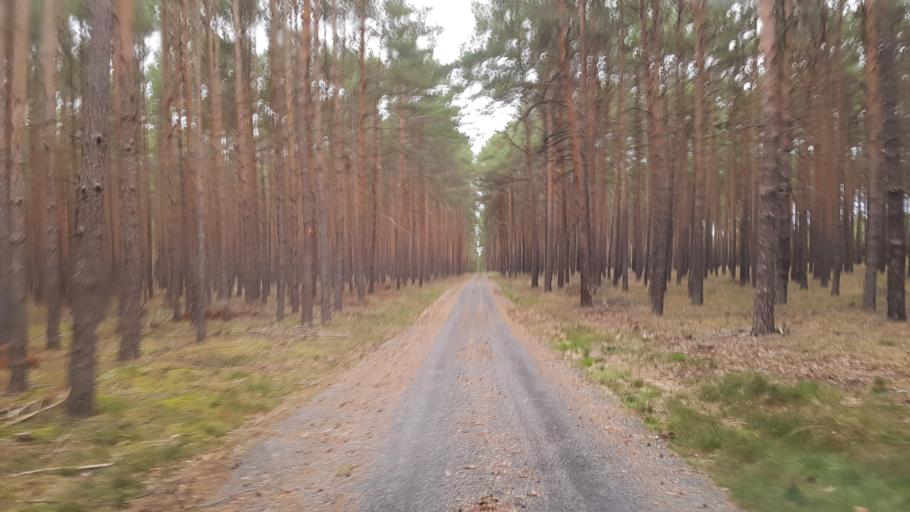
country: DE
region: Brandenburg
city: Sonnewalde
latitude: 51.7275
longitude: 13.6642
